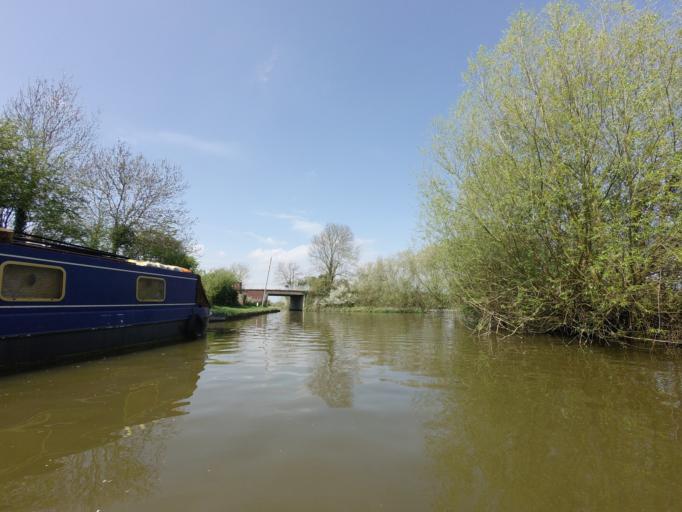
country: GB
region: England
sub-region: Buckinghamshire
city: Cheddington
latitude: 51.8723
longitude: -0.6503
